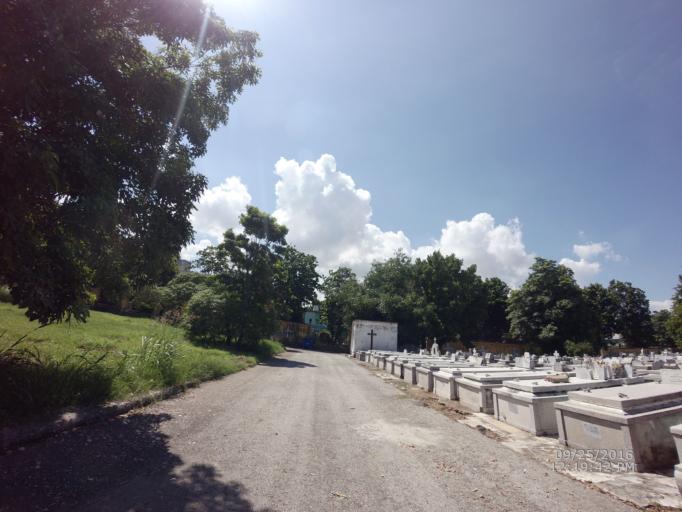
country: CU
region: La Habana
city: Havana
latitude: 23.1205
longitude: -82.3976
